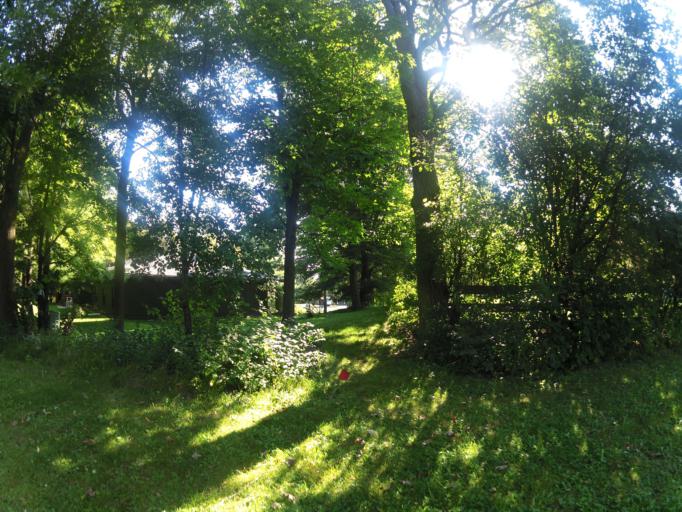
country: CA
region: Ontario
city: Bells Corners
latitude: 45.3284
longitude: -75.9117
